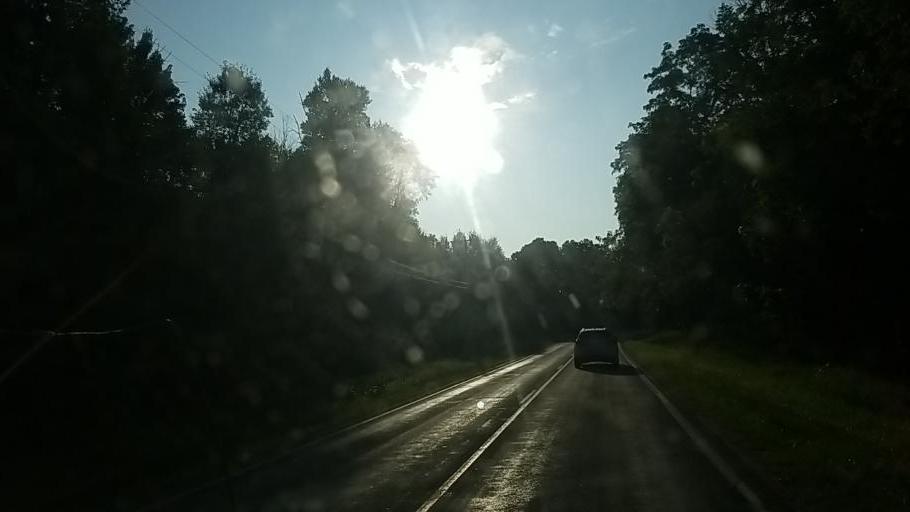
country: US
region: Michigan
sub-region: Montcalm County
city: Stanton
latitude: 43.2498
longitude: -85.0800
